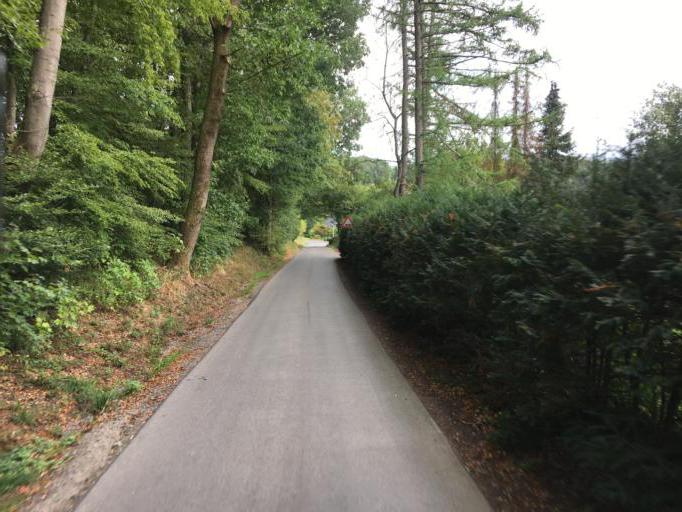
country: DE
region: North Rhine-Westphalia
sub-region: Regierungsbezirk Arnsberg
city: Herscheid
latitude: 51.2048
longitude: 7.7791
